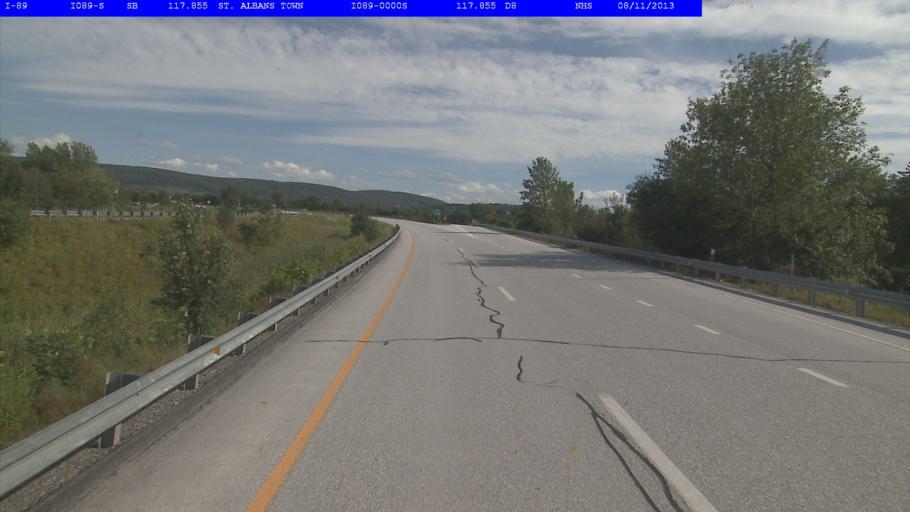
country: US
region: Vermont
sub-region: Franklin County
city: Saint Albans
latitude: 44.8461
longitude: -73.0826
